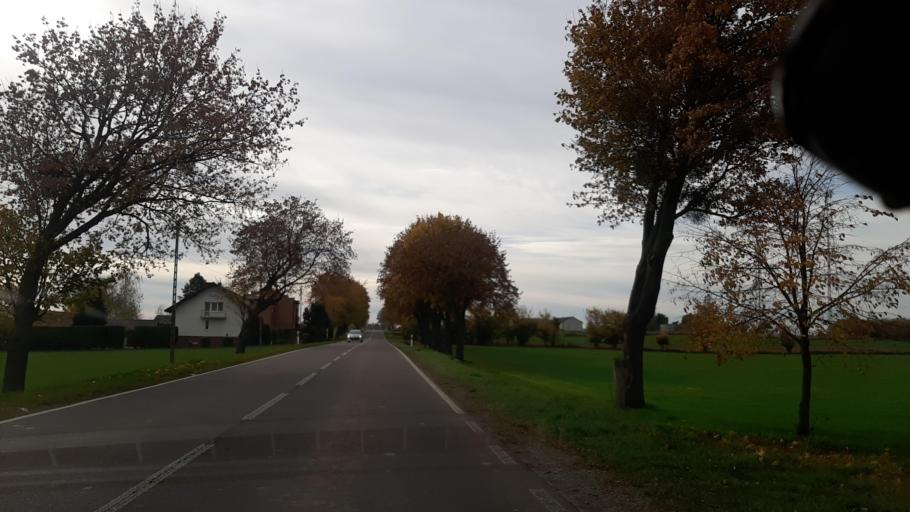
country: PL
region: Lublin Voivodeship
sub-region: Powiat pulawski
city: Markuszow
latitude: 51.3407
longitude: 22.2590
